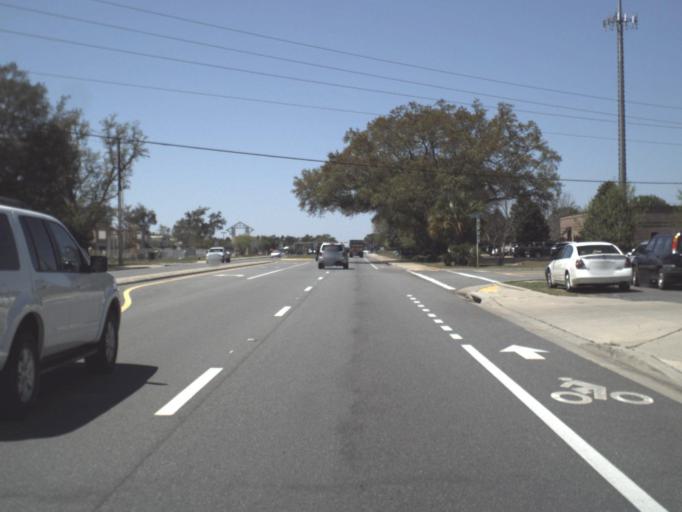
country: US
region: Florida
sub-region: Okaloosa County
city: Niceville
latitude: 30.4789
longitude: -86.4100
